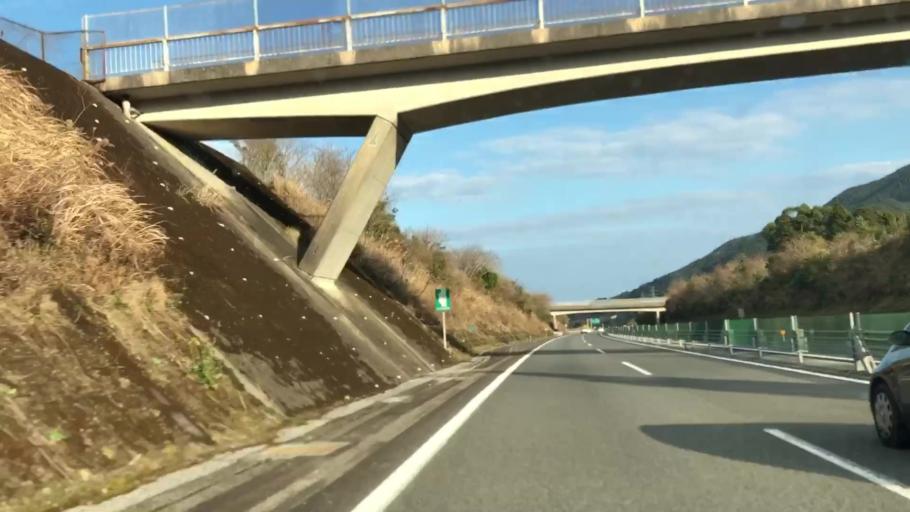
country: JP
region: Miyazaki
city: Miyazaki-shi
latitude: 31.8326
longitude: 131.3235
